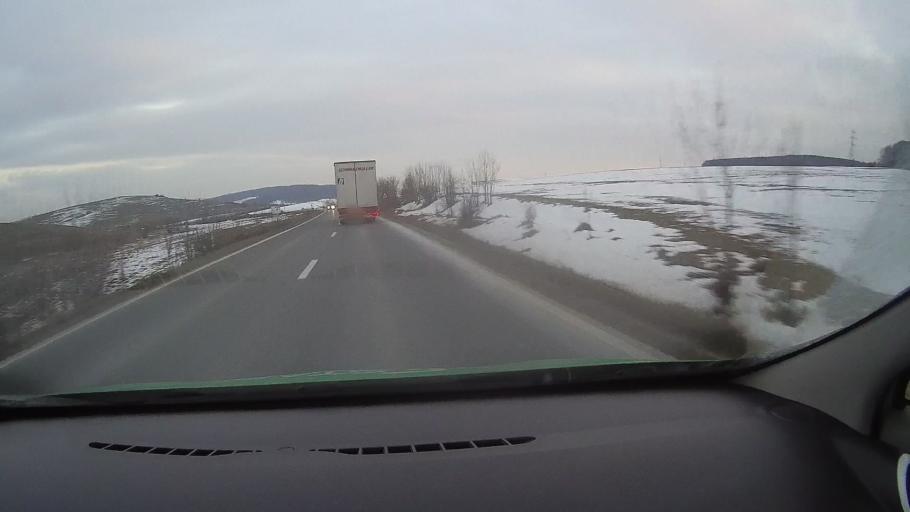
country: RO
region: Harghita
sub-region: Comuna Lupeni
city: Lupeni
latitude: 46.3525
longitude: 25.2555
